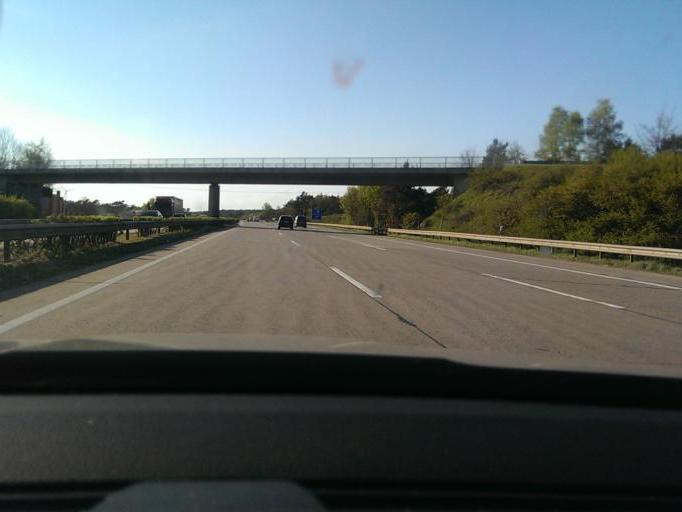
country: DE
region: Lower Saxony
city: Elze
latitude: 52.5717
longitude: 9.7807
